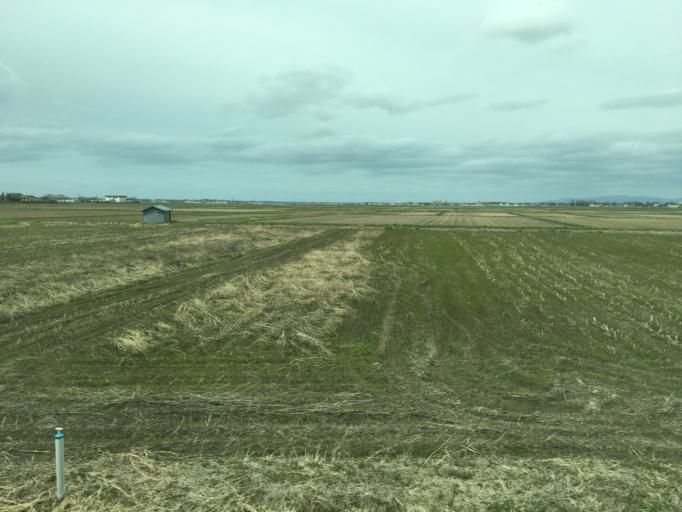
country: JP
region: Aomori
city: Goshogawara
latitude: 40.8095
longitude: 140.4189
